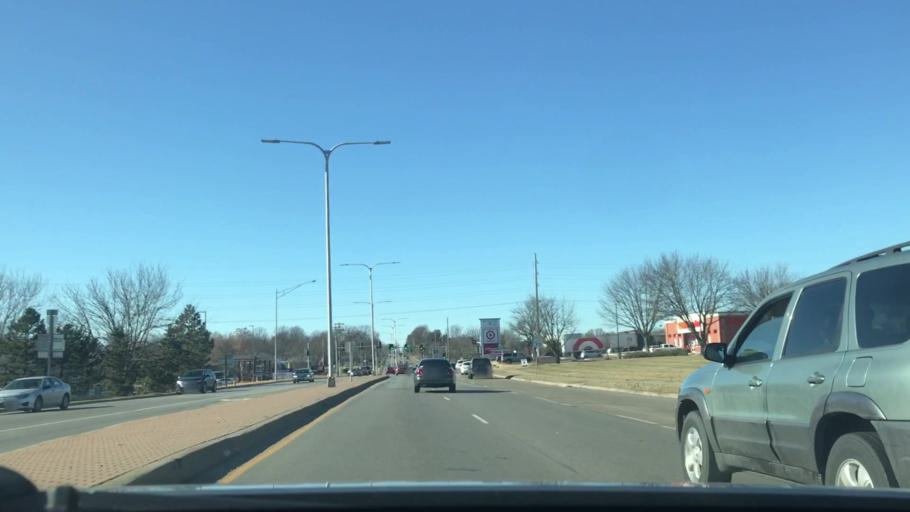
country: US
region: Missouri
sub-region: Jackson County
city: East Independence
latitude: 39.0483
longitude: -94.3665
